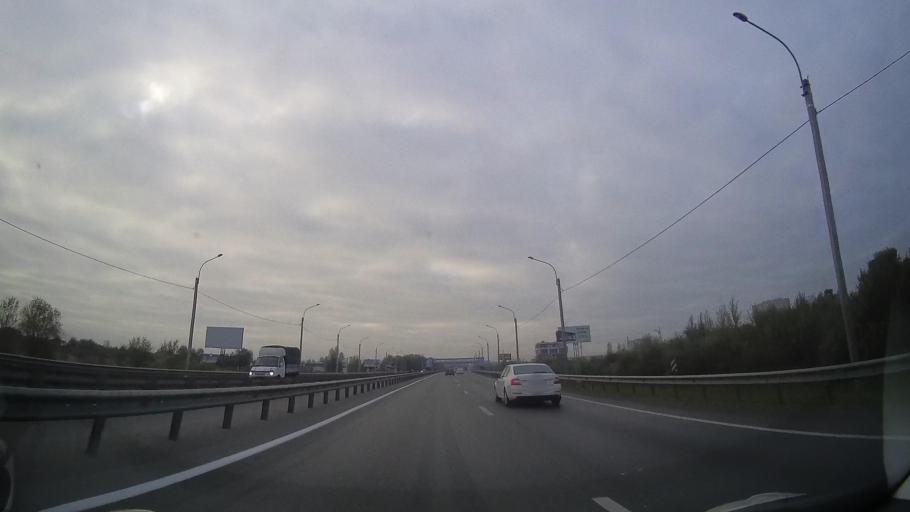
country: RU
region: Rostov
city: Bataysk
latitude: 47.1425
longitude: 39.7758
